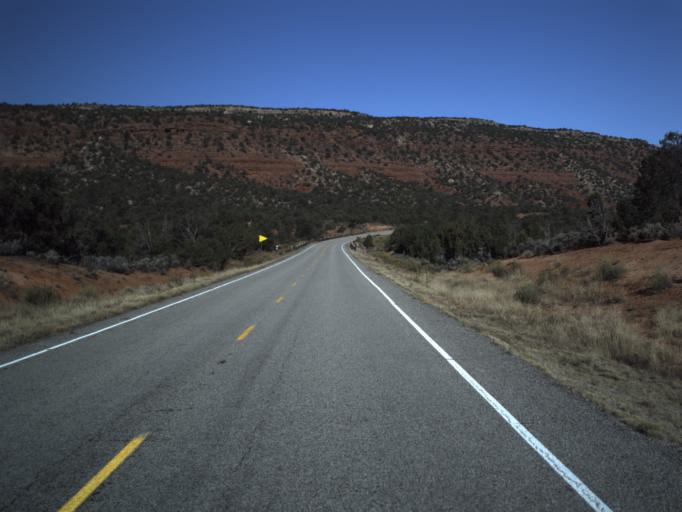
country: US
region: Utah
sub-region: San Juan County
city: Blanding
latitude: 37.5668
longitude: -110.0319
